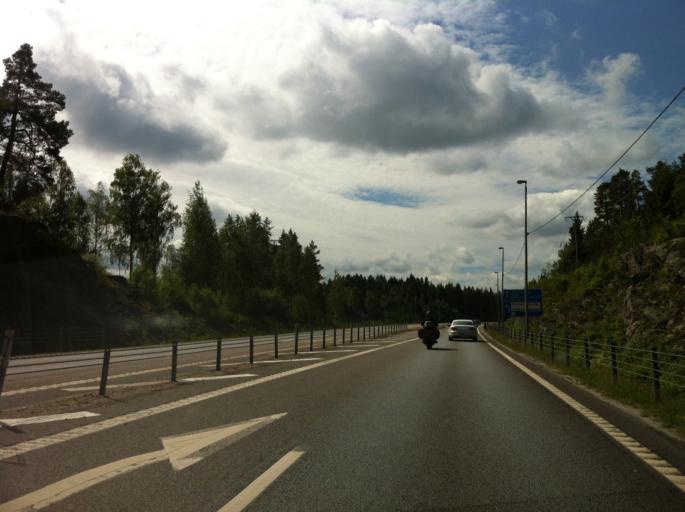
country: SE
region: Vaermland
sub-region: Grums Kommun
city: Grums
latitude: 59.3557
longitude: 13.1313
